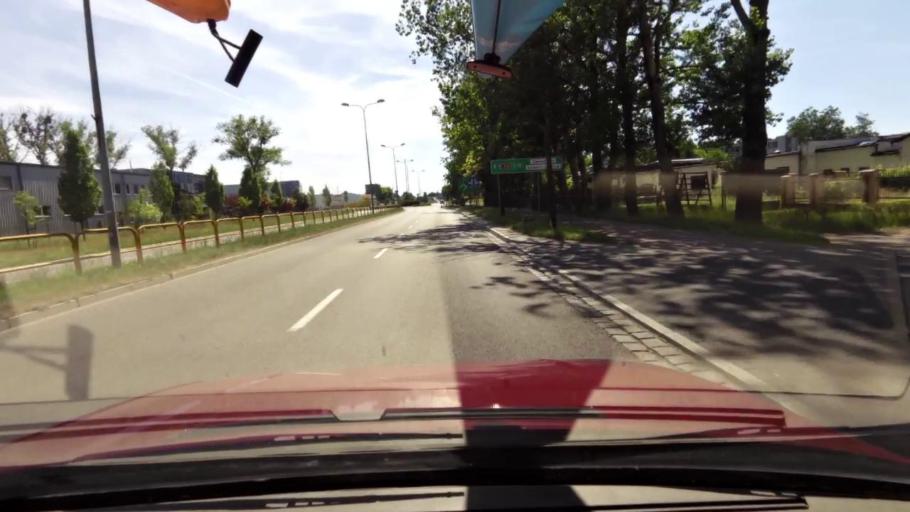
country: PL
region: Pomeranian Voivodeship
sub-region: Slupsk
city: Slupsk
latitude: 54.4509
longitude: 17.0146
